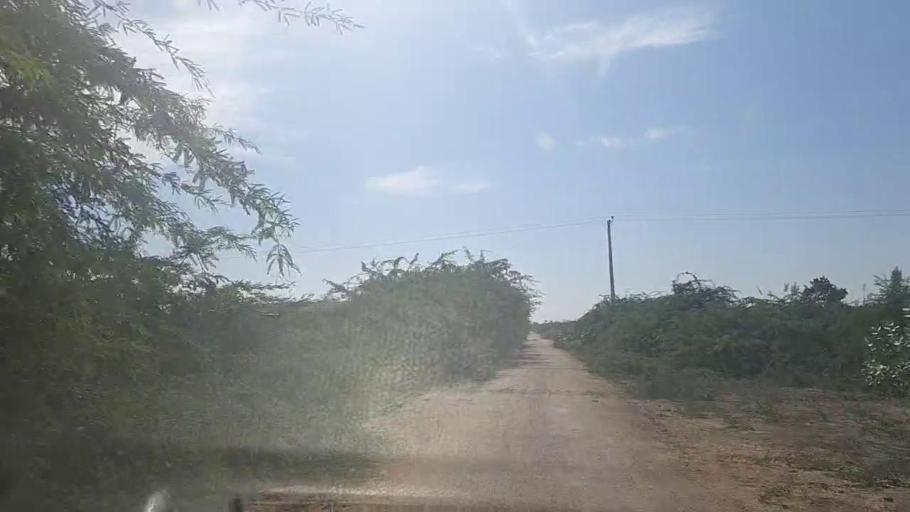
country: PK
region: Sindh
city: Mirpur Batoro
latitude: 24.6730
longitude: 68.1831
